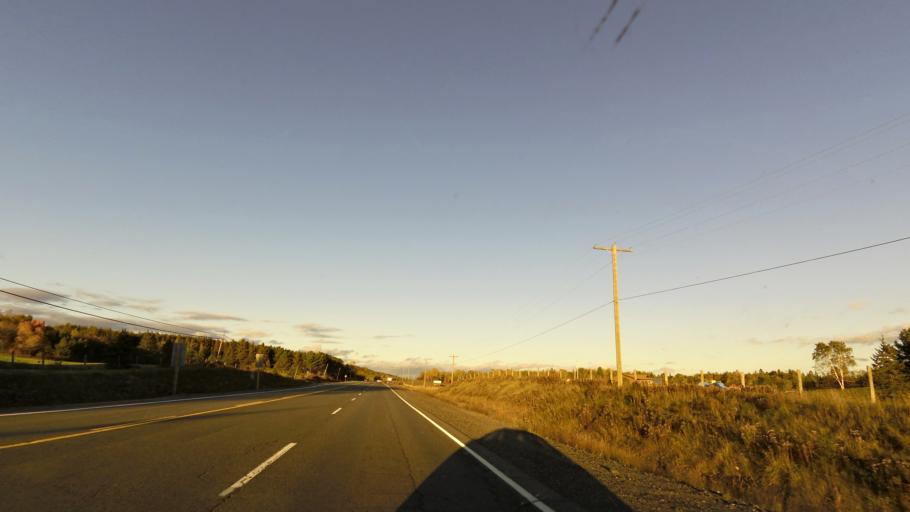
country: CA
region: Ontario
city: Espanola
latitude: 46.3452
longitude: -81.4631
